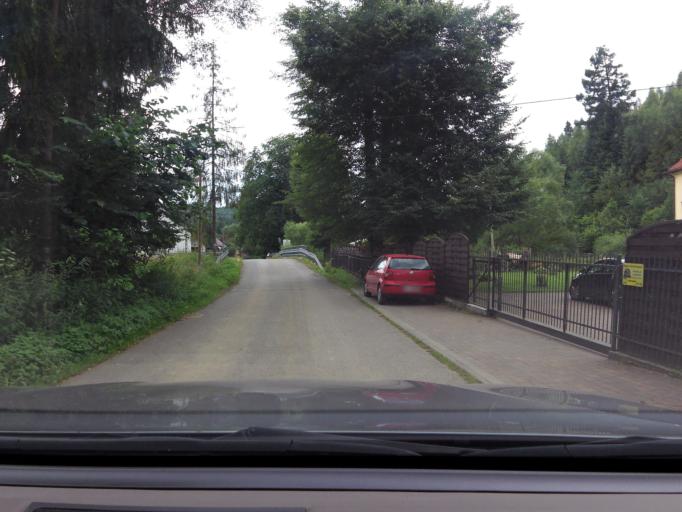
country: PL
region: Silesian Voivodeship
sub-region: Powiat zywiecki
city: Ujsoly
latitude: 49.5037
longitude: 19.1365
